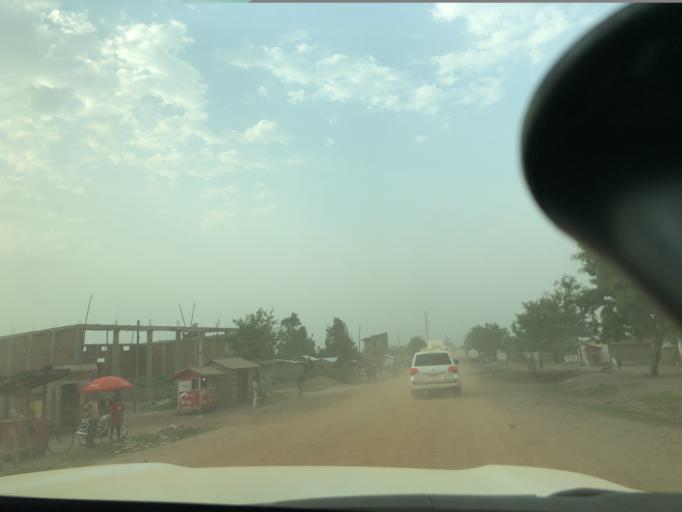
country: UG
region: Western Region
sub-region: Kasese District
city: Margherita
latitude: 0.3273
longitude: 29.6765
